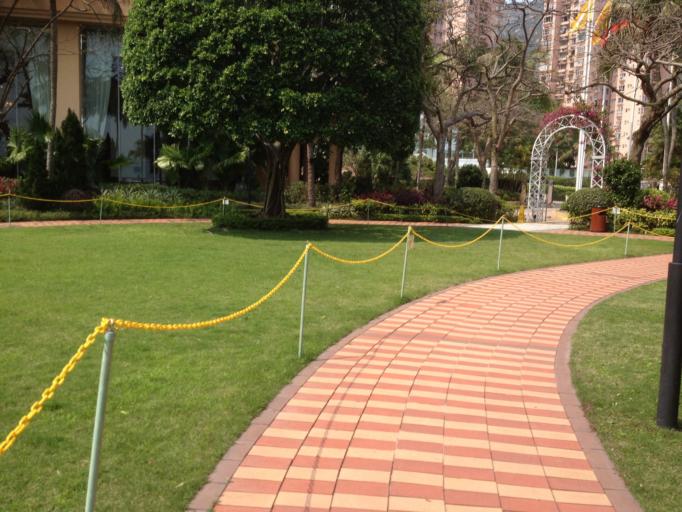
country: HK
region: Tuen Mun
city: Tuen Mun
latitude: 22.3719
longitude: 113.9904
